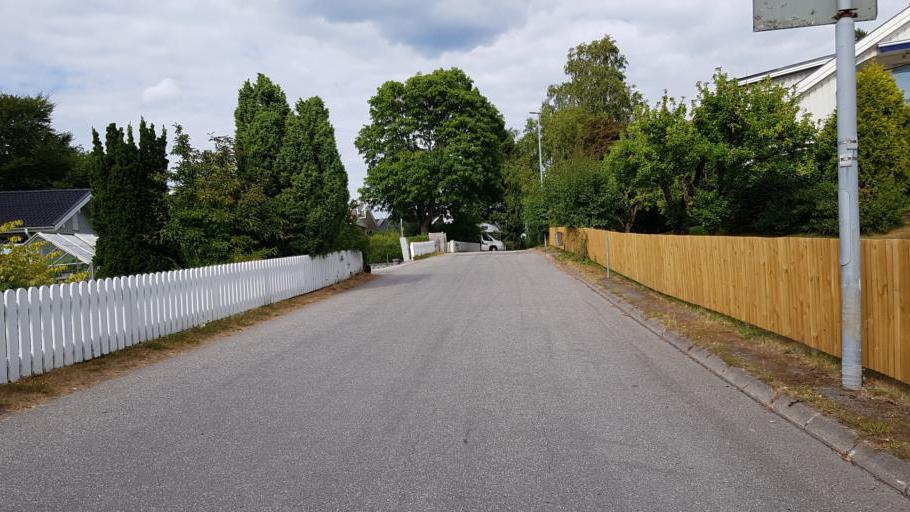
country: SE
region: Vaestra Goetaland
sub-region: Partille Kommun
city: Furulund
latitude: 57.7084
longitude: 12.1444
